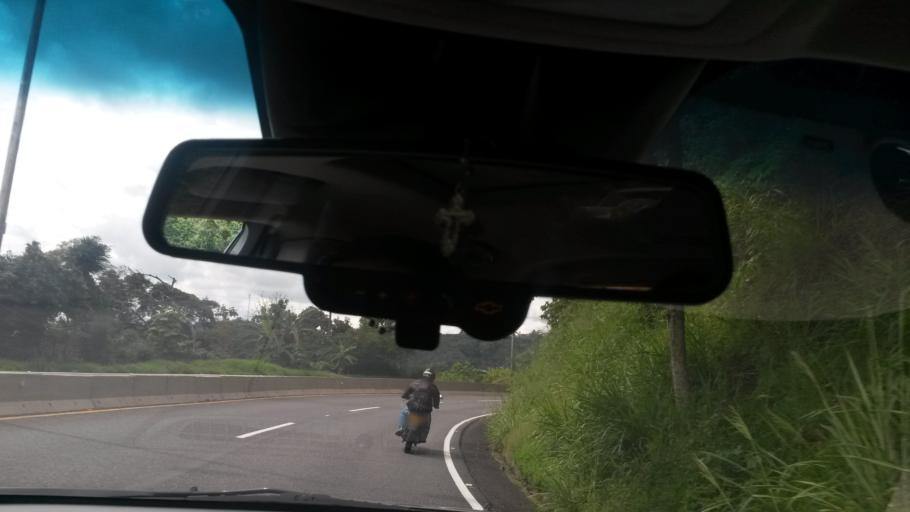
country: CO
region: Caldas
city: Manizales
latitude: 5.0599
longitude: -75.5544
